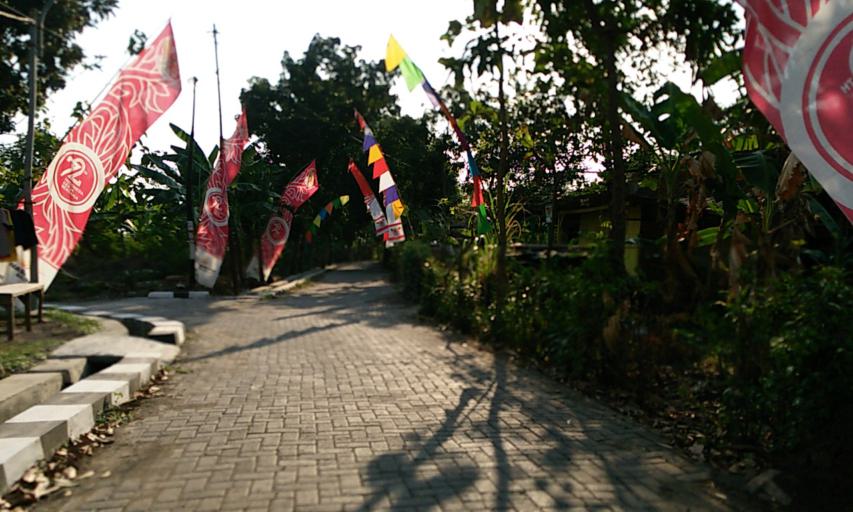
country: ID
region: Central Java
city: Mranggen
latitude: -7.0069
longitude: 110.4877
